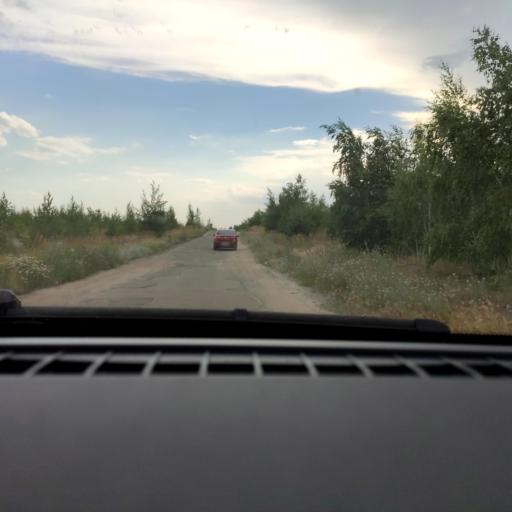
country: RU
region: Voronezj
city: Somovo
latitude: 51.7701
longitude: 39.3347
